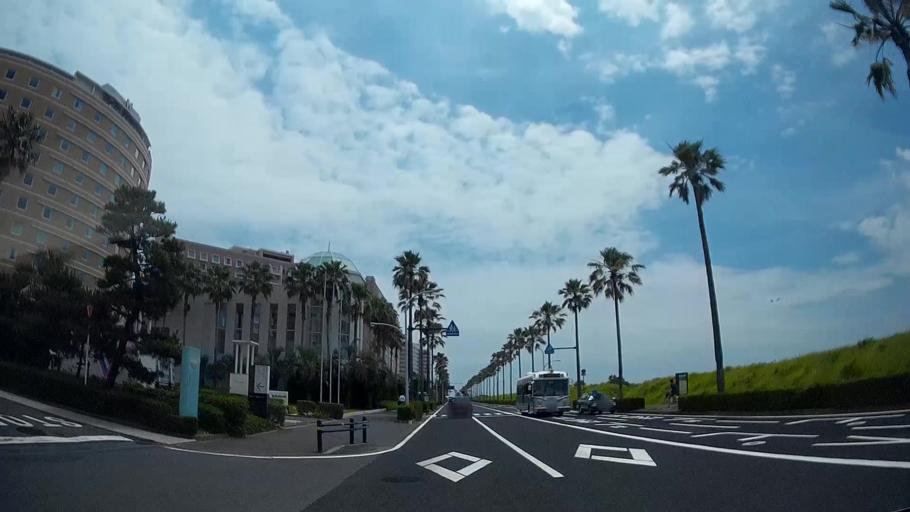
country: JP
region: Tokyo
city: Urayasu
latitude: 35.6314
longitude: 139.8730
